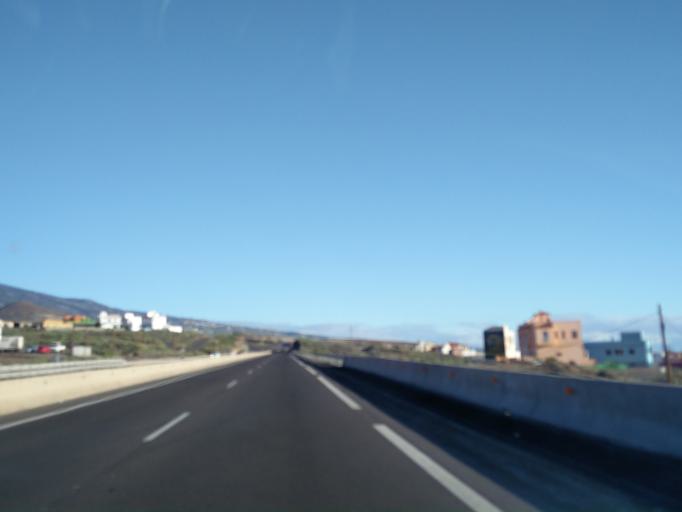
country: ES
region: Canary Islands
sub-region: Provincia de Santa Cruz de Tenerife
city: Fasnia
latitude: 28.1912
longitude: -16.4275
